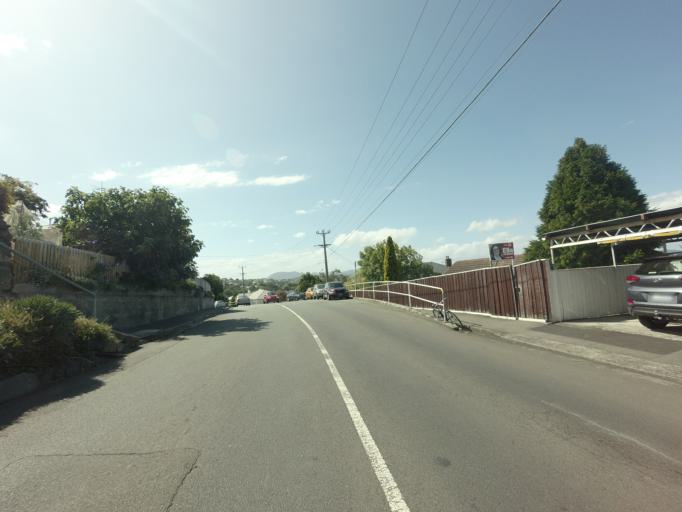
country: AU
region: Tasmania
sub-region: Hobart
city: Dynnyrne
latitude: -42.9032
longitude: 147.3193
